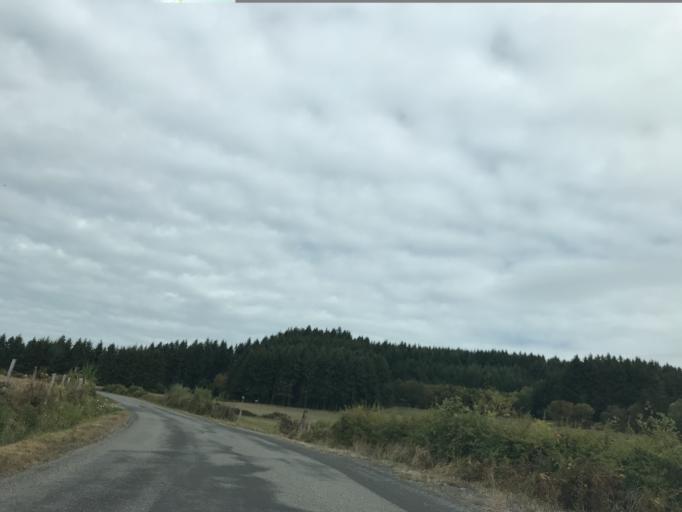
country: FR
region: Auvergne
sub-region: Departement du Puy-de-Dome
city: Thiers
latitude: 45.8364
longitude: 3.5630
